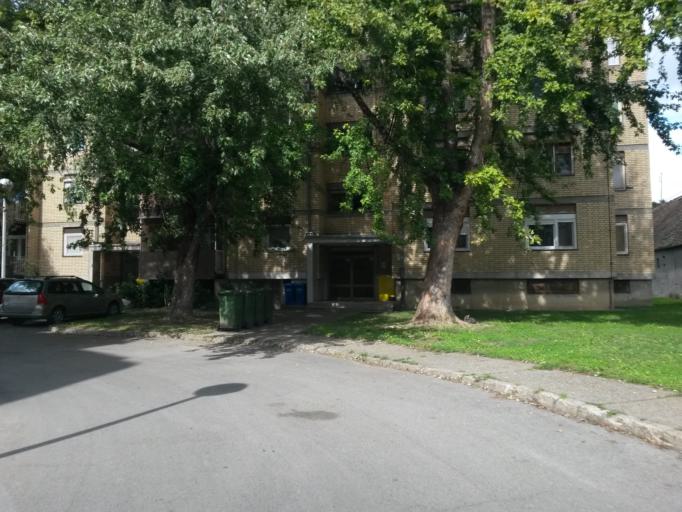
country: HR
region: Osjecko-Baranjska
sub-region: Grad Osijek
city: Osijek
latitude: 45.5617
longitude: 18.6705
